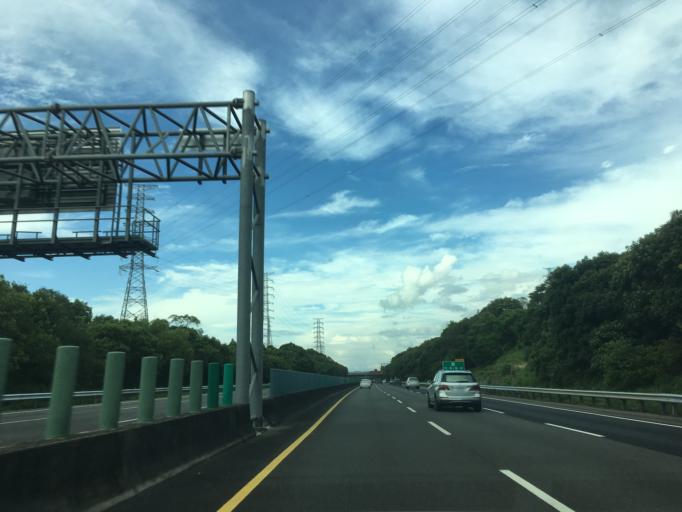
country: TW
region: Taiwan
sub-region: Chiayi
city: Jiayi Shi
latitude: 23.5843
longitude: 120.5133
